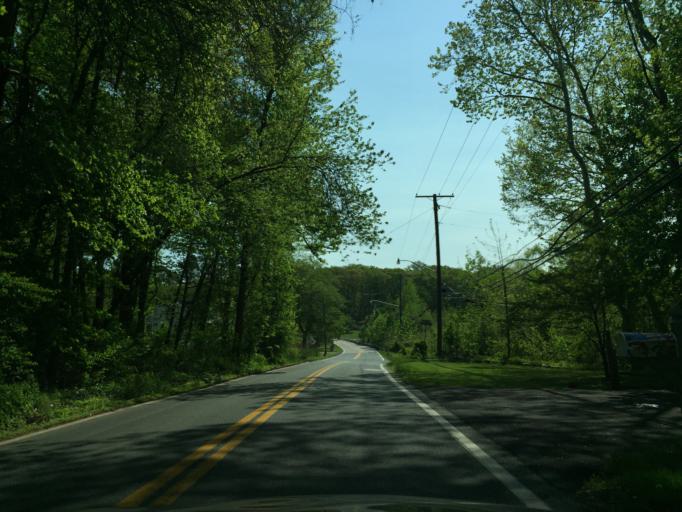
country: US
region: Maryland
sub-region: Baltimore County
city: White Marsh
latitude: 39.3663
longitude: -76.4157
